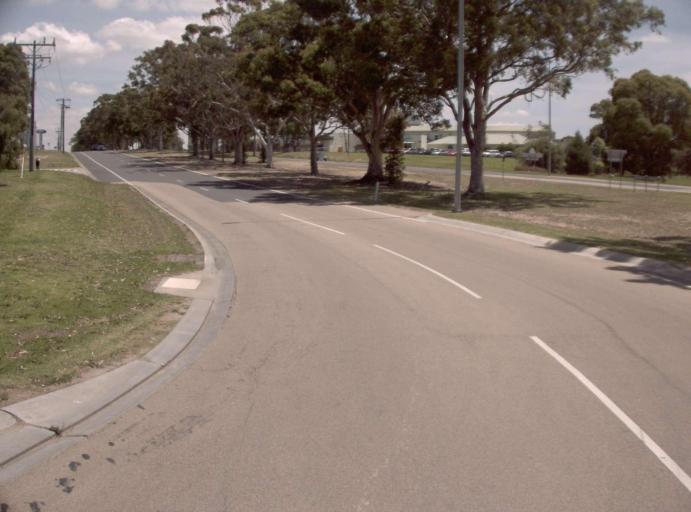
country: AU
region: Victoria
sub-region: East Gippsland
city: Bairnsdale
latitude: -37.8313
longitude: 147.6110
